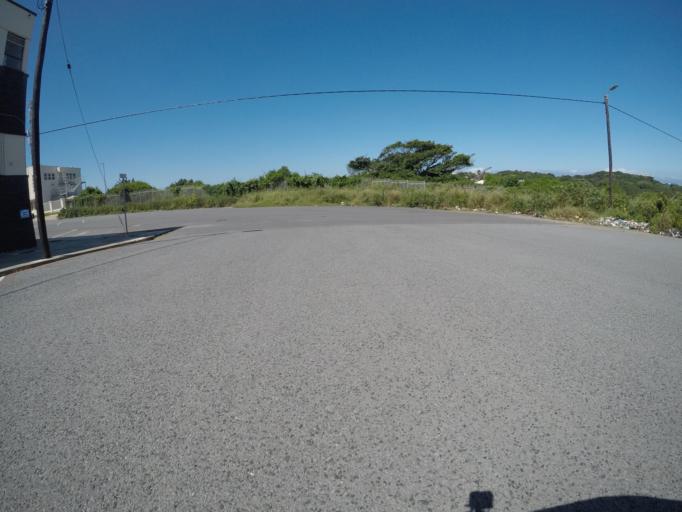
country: ZA
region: Eastern Cape
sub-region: Buffalo City Metropolitan Municipality
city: East London
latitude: -33.0215
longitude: 27.9075
